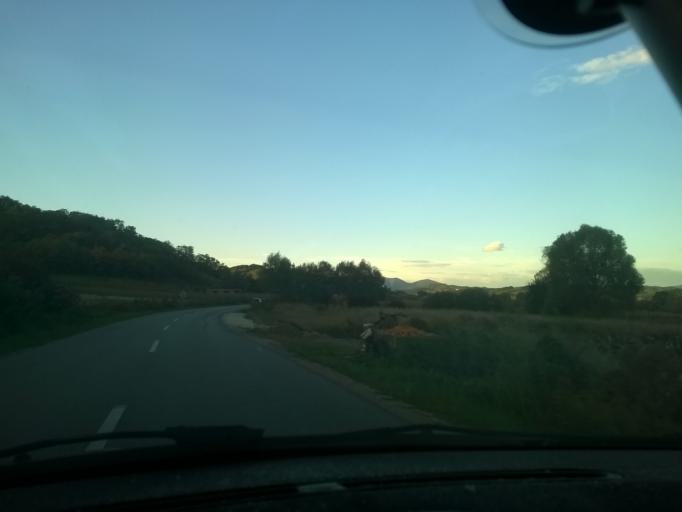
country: HR
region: Krapinsko-Zagorska
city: Zabok
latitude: 46.0491
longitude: 15.9085
